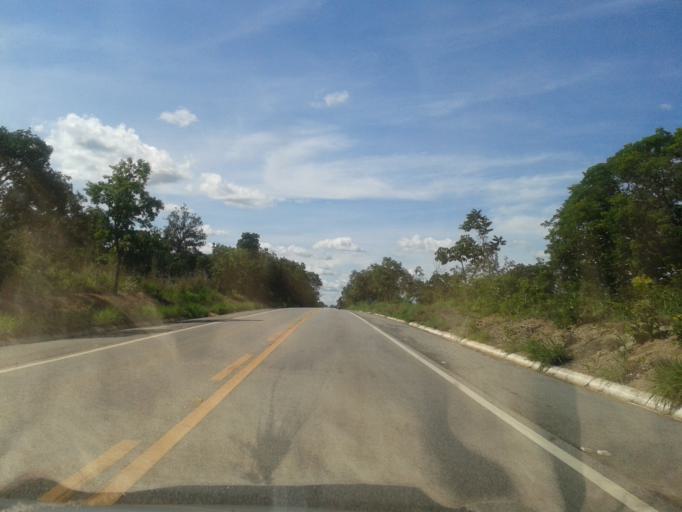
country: BR
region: Goias
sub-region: Mozarlandia
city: Mozarlandia
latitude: -15.2805
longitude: -50.4761
